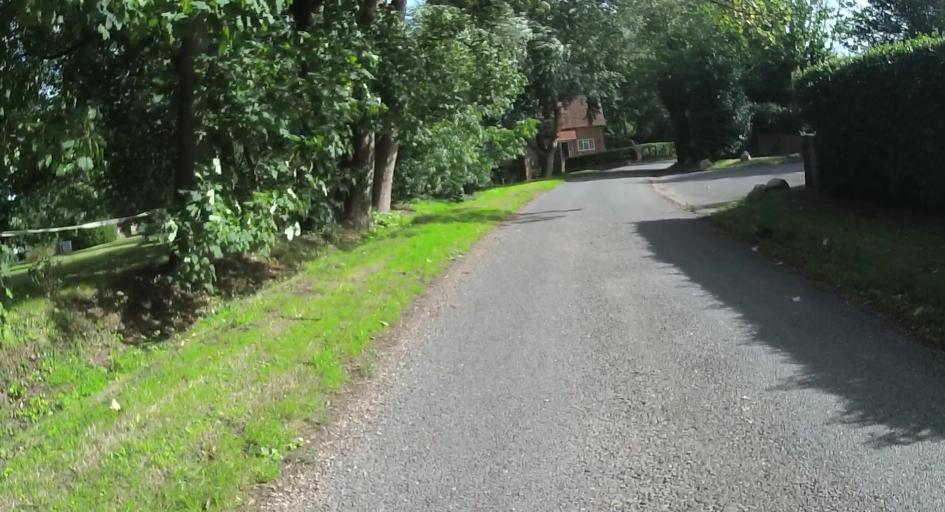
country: GB
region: England
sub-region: Hampshire
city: Kingsclere
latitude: 51.3722
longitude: -1.2087
